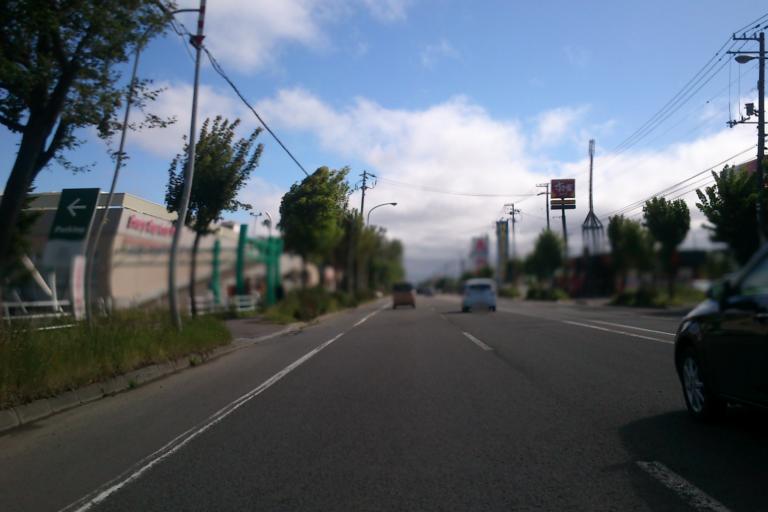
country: JP
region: Hokkaido
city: Sapporo
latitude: 43.1479
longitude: 141.2826
